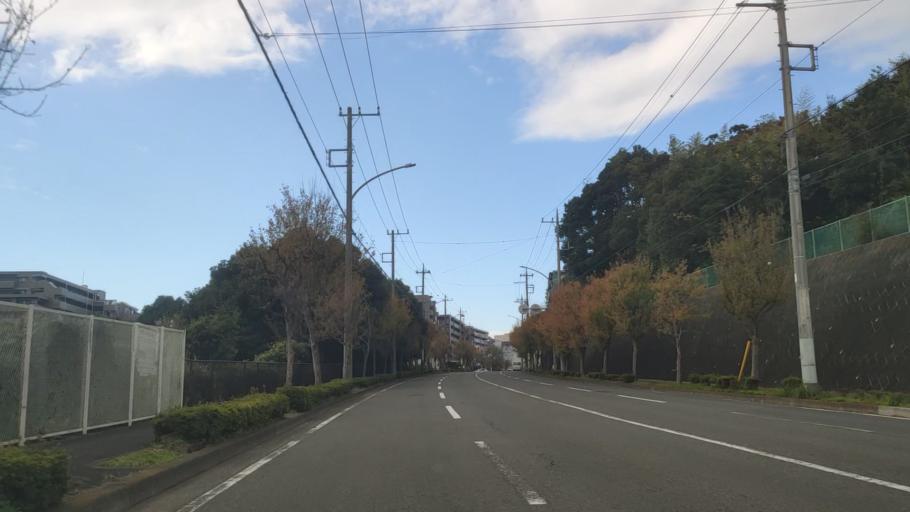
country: JP
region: Kanagawa
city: Minami-rinkan
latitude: 35.4274
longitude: 139.5144
